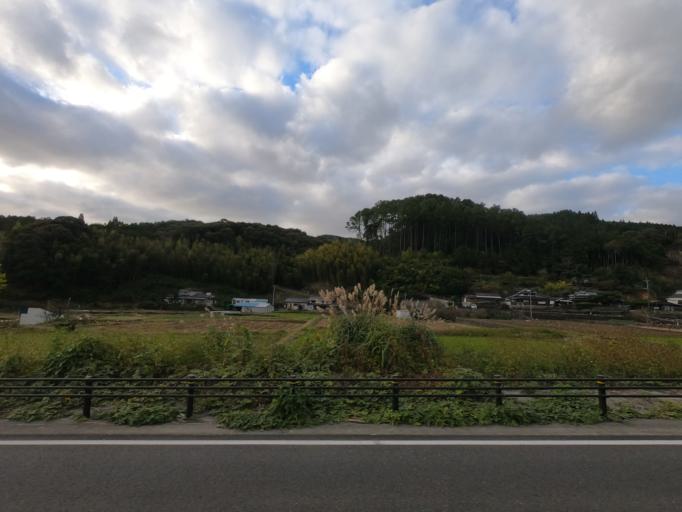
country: JP
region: Kumamoto
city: Minamata
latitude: 32.2427
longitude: 130.4684
